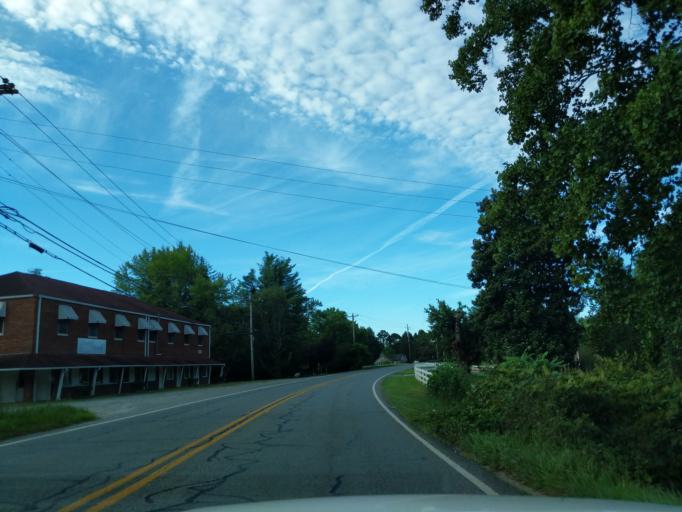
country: US
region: Georgia
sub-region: Fannin County
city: McCaysville
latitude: 34.9664
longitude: -84.3701
